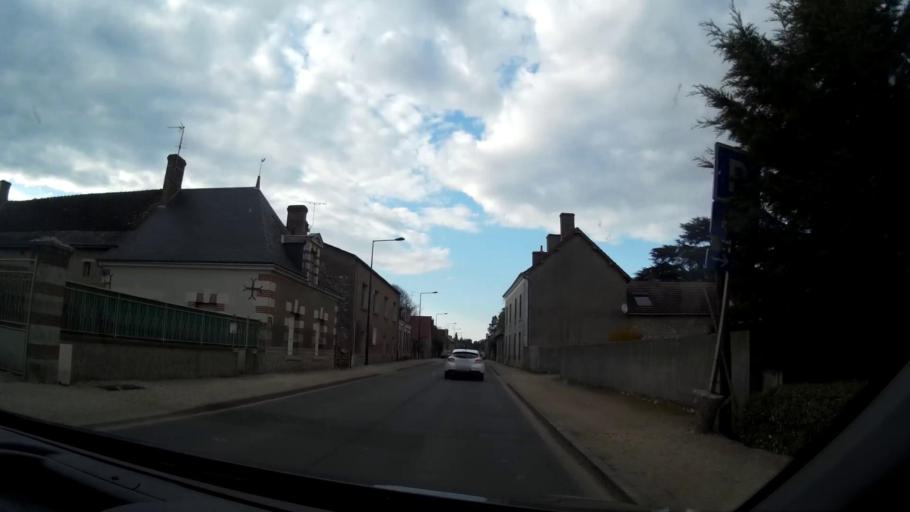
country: FR
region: Centre
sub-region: Departement du Loir-et-Cher
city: Cormeray
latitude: 47.4900
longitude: 1.4071
